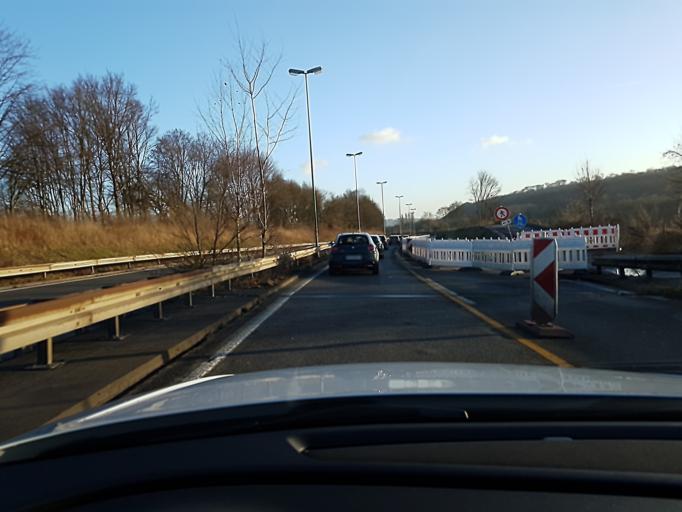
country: DE
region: North Rhine-Westphalia
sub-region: Regierungsbezirk Dusseldorf
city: Essen
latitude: 51.4272
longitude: 7.0592
